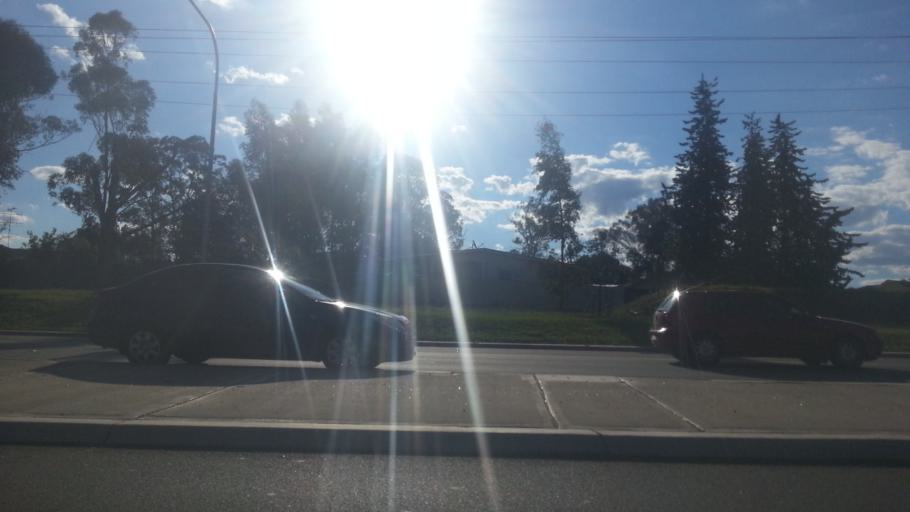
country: AU
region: New South Wales
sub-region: Penrith Municipality
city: Werrington Downs
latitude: -33.7330
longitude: 150.7180
